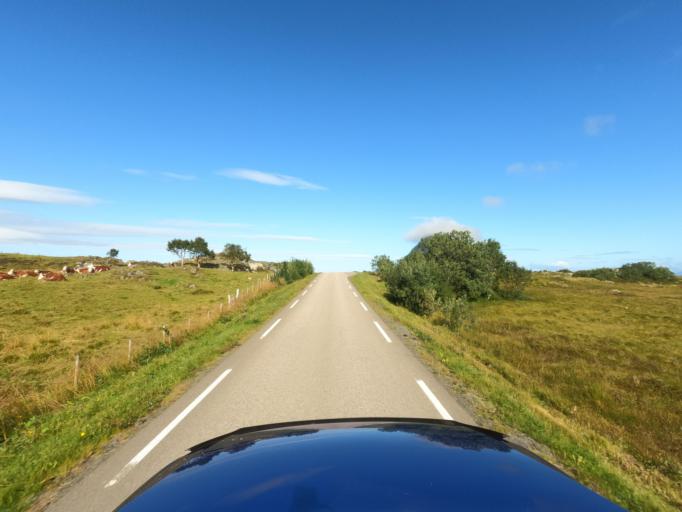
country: NO
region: Nordland
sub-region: Vestvagoy
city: Evjen
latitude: 68.3072
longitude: 14.0980
